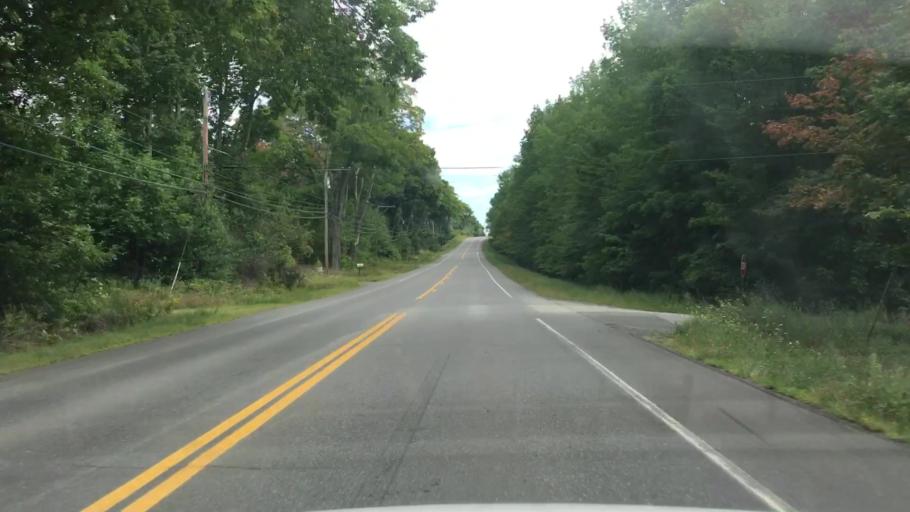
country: US
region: Maine
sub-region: Piscataquis County
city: Brownville
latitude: 45.2271
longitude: -69.1136
